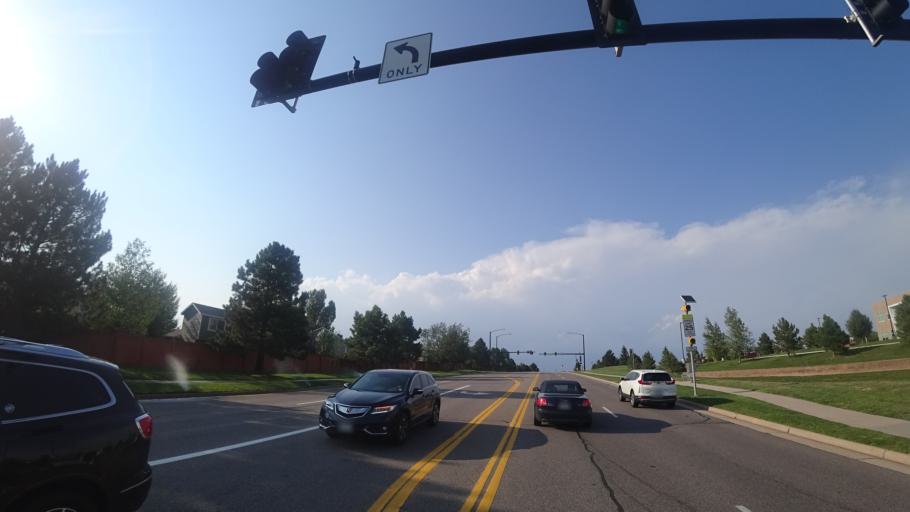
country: US
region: Colorado
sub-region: Arapahoe County
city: Dove Valley
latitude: 39.6191
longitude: -104.7387
